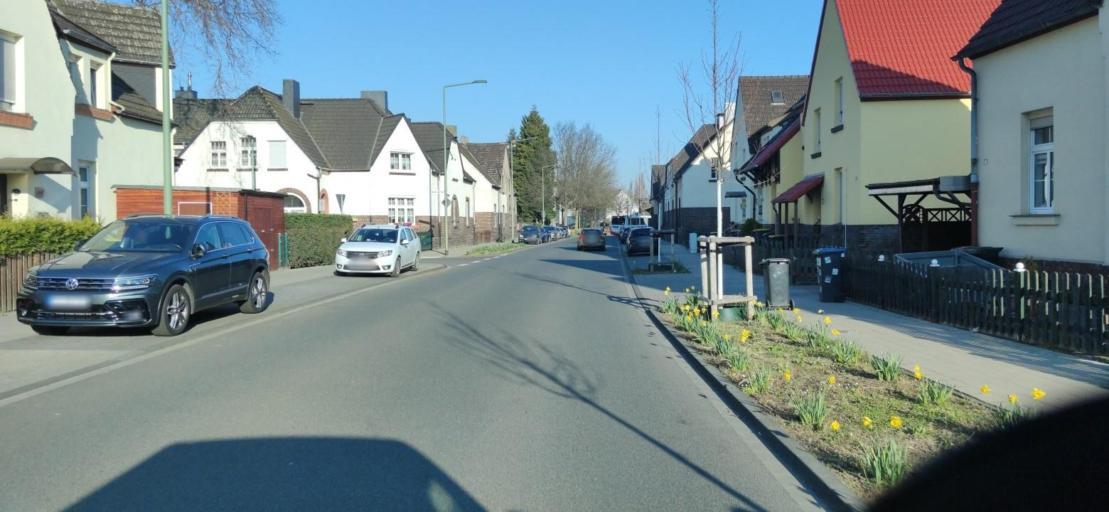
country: DE
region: North Rhine-Westphalia
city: Meiderich
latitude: 51.4963
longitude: 6.7884
